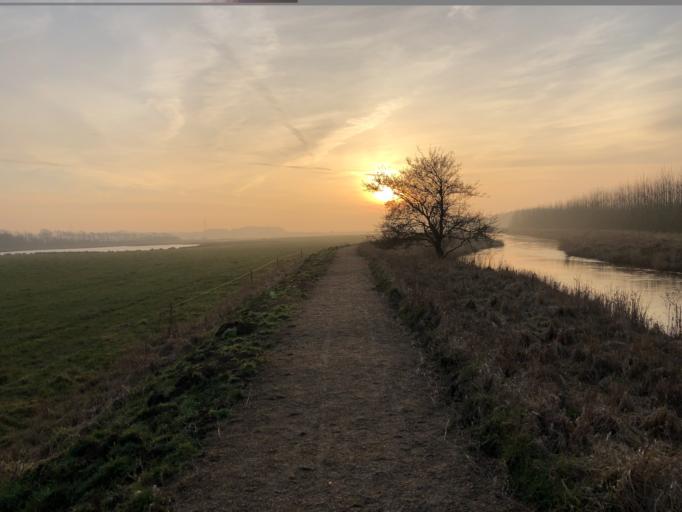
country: DK
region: Central Jutland
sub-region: Holstebro Kommune
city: Ulfborg
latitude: 56.3420
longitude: 8.3626
